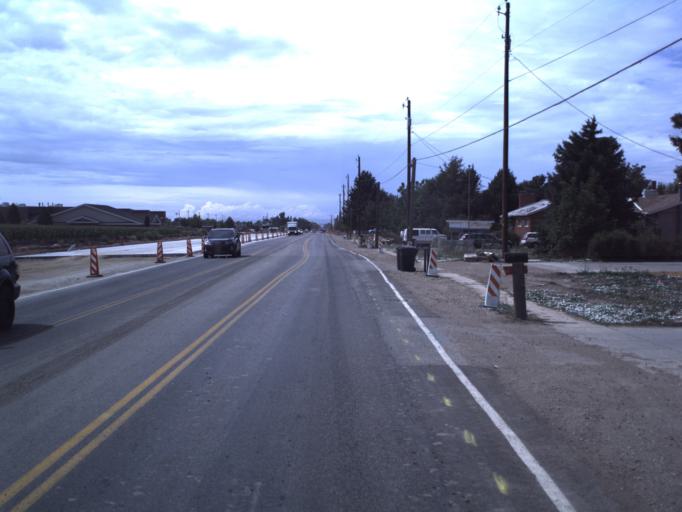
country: US
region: Utah
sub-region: Davis County
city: Syracuse
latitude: 41.1092
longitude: -112.0646
